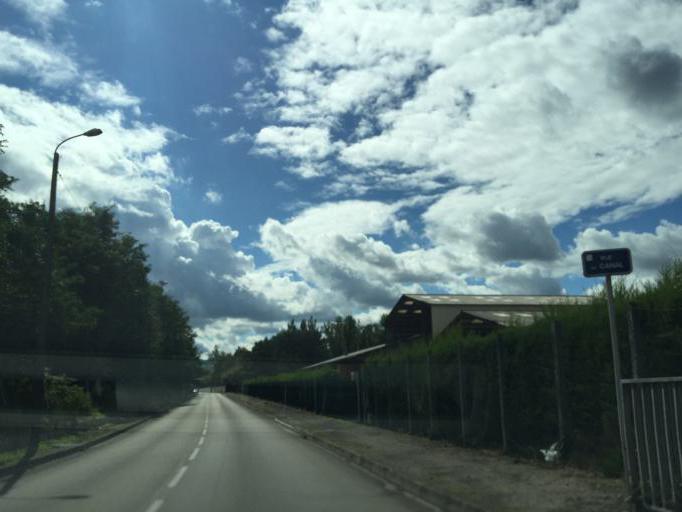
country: FR
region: Rhone-Alpes
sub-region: Departement de la Loire
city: Lorette
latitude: 45.5100
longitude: 4.5719
